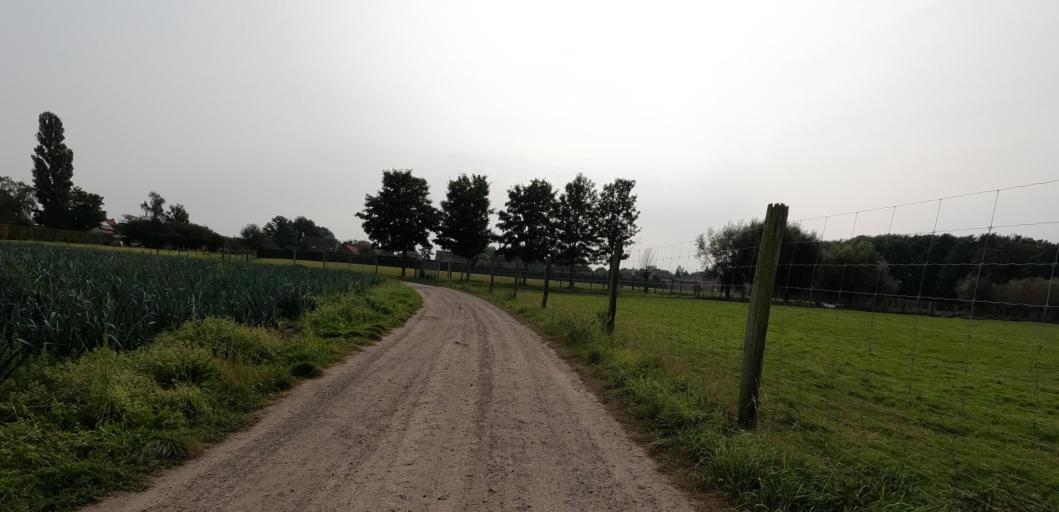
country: BE
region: Flanders
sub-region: Provincie Antwerpen
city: Sint-Amands
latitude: 51.0436
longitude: 4.1930
